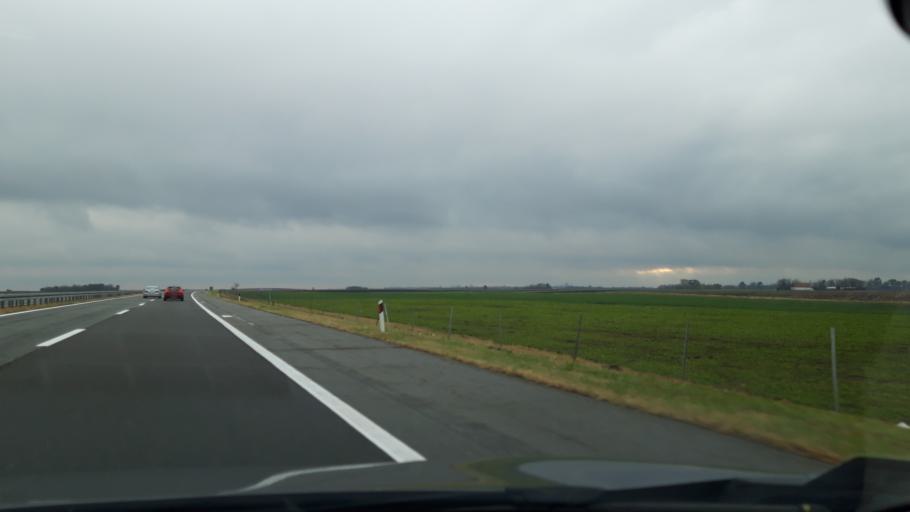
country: RS
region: Autonomna Pokrajina Vojvodina
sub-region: Severnobacki Okrug
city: Backa Topola
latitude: 45.8632
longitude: 19.6992
